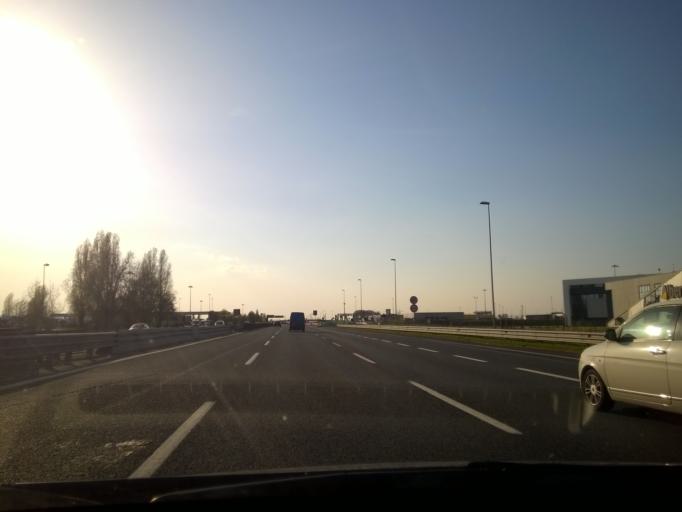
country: IT
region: Emilia-Romagna
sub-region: Provincia di Bologna
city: Castel San Pietro Terme
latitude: 44.4279
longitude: 11.6016
